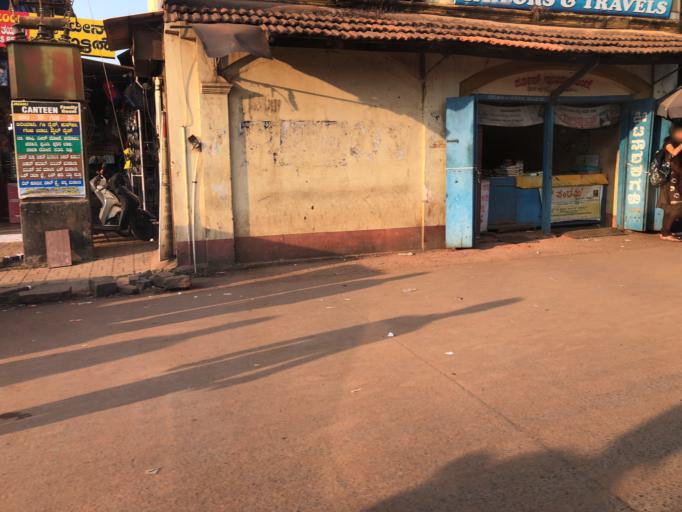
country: IN
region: Karnataka
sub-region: Dakshina Kannada
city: Mangalore
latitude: 12.8639
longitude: 74.8368
